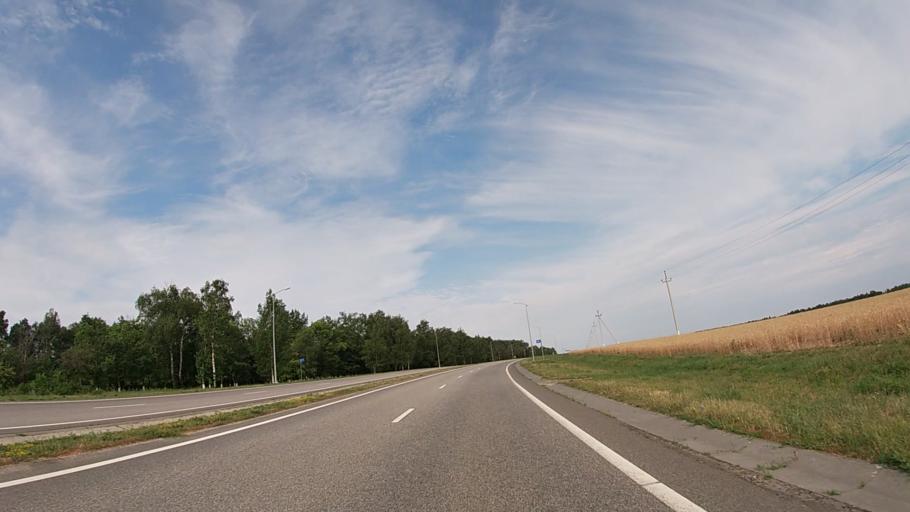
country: RU
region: Belgorod
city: Borisovka
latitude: 50.7497
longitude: 35.9903
